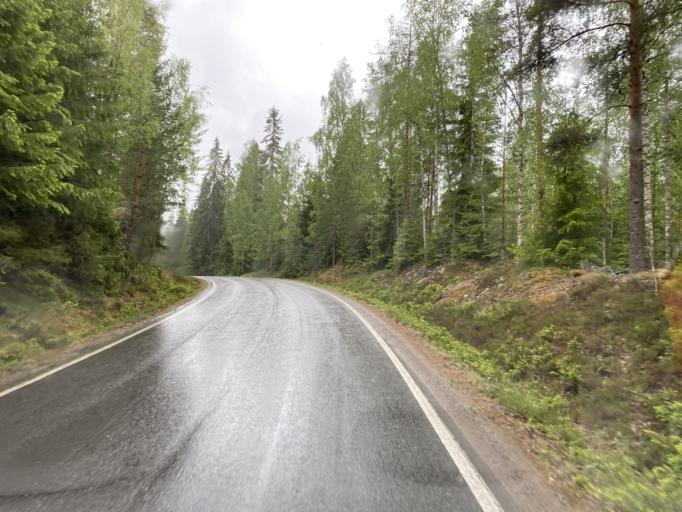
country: FI
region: Haeme
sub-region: Forssa
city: Humppila
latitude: 61.0773
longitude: 23.3103
